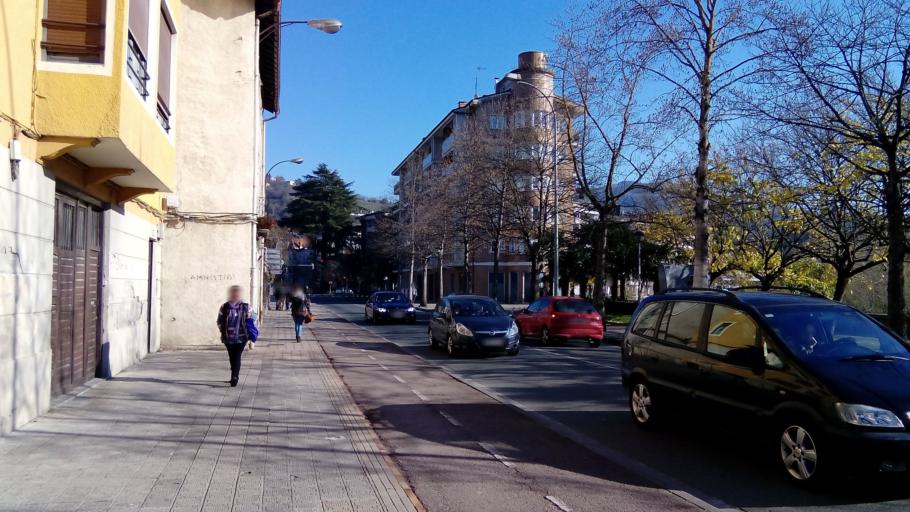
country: ES
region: Basque Country
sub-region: Provincia de Guipuzcoa
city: Tolosa
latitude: 43.1337
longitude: -2.0803
